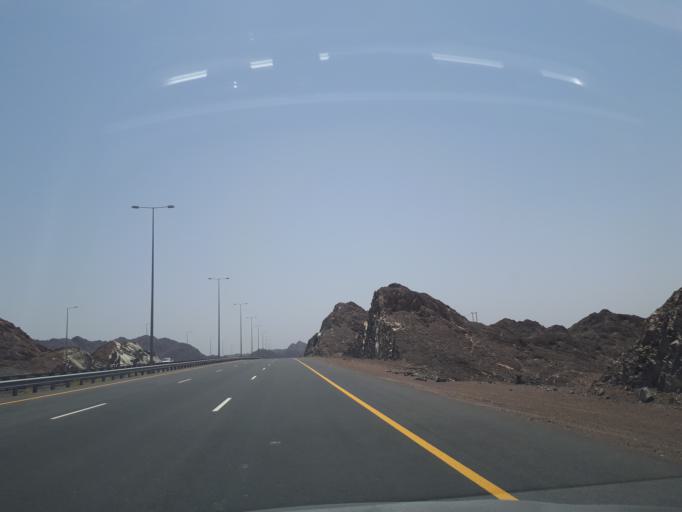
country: OM
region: Ash Sharqiyah
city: Ibra'
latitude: 22.7328
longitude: 58.5605
